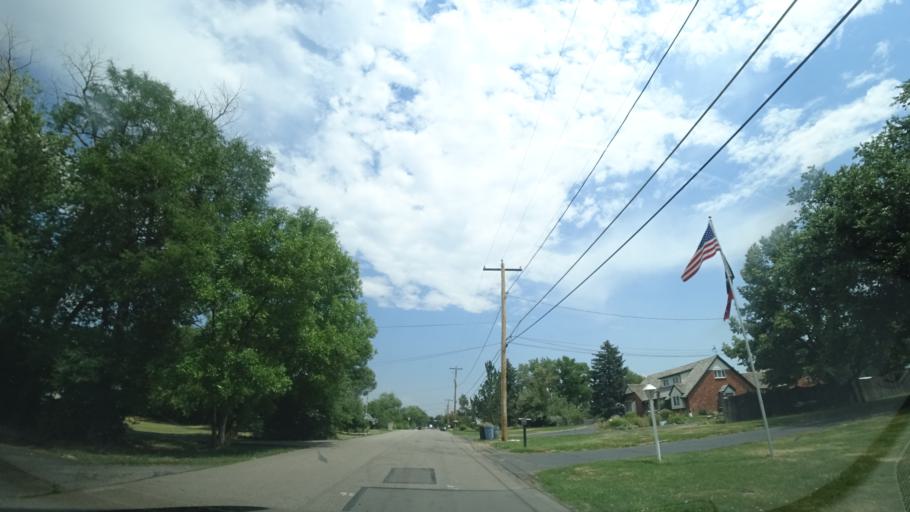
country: US
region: Colorado
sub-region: Jefferson County
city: Lakewood
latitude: 39.7238
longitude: -105.0850
